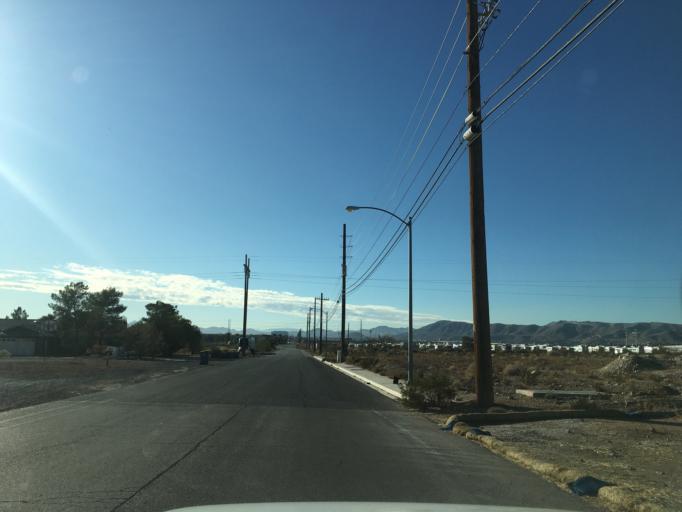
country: US
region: Nevada
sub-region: Clark County
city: Enterprise
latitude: 36.0112
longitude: -115.1702
